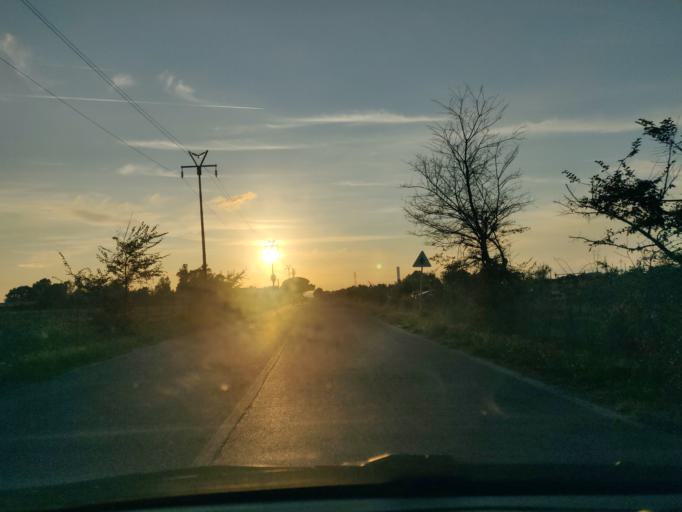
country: IT
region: Latium
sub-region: Citta metropolitana di Roma Capitale
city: Aurelia
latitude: 42.1330
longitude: 11.8085
